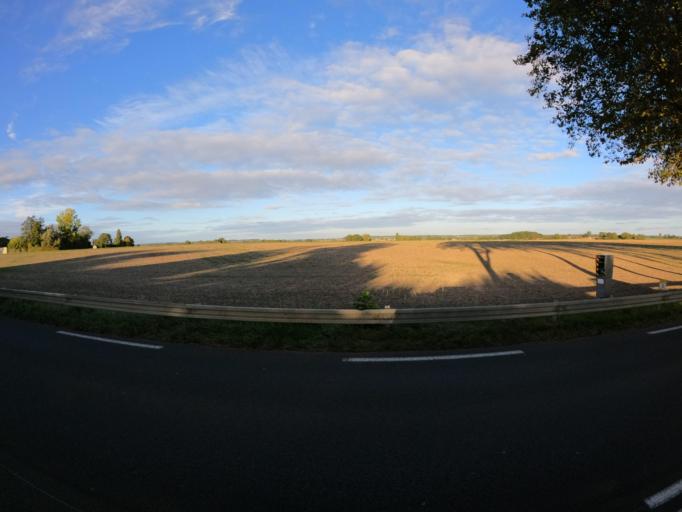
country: FR
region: Pays de la Loire
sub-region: Departement de Maine-et-Loire
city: Brissac-Quince
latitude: 47.3138
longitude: -0.4029
